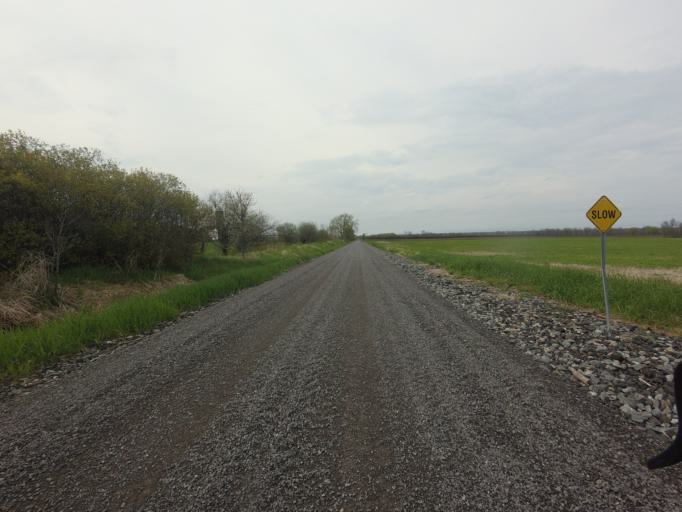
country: CA
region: Ontario
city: Carleton Place
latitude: 45.1894
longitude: -76.1613
